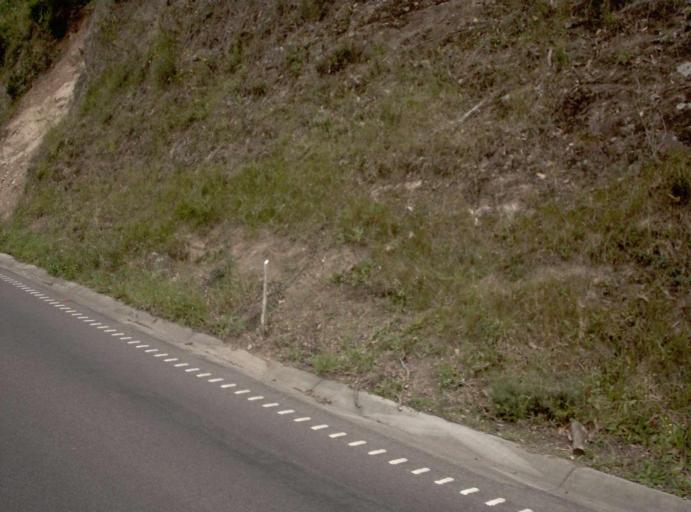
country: AU
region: Victoria
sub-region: Yarra Ranges
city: Yarra Glen
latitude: -37.5340
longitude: 145.4145
